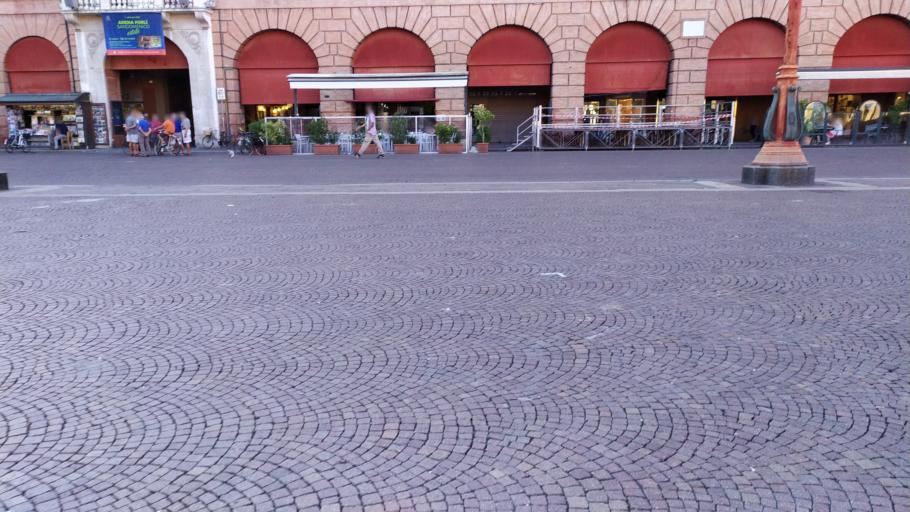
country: IT
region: Emilia-Romagna
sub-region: Forli-Cesena
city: Forli
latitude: 44.2225
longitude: 12.0407
